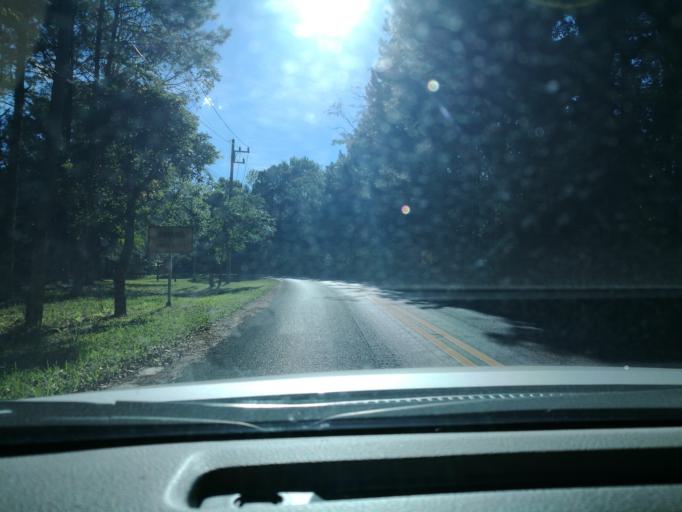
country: TH
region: Phitsanulok
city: Nakhon Thai
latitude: 16.9955
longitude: 101.0132
